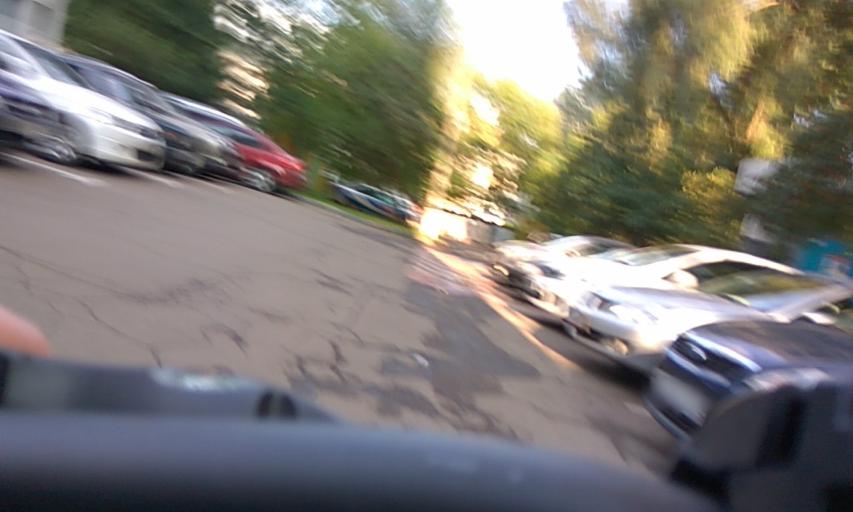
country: RU
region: Moscow
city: Kolomenskoye
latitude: 55.6780
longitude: 37.6986
